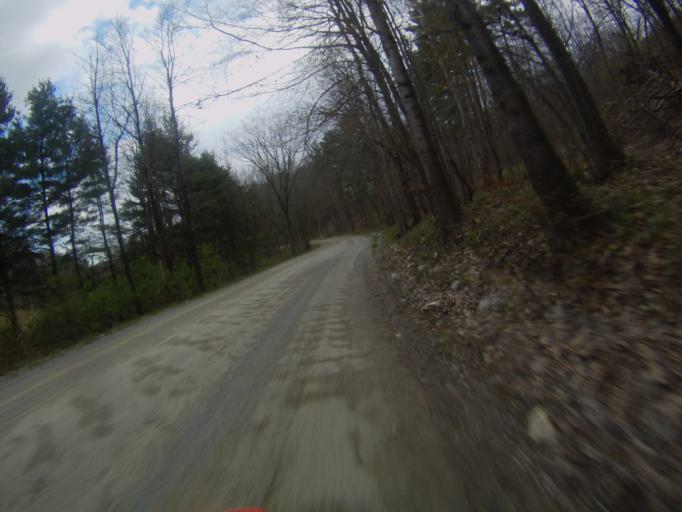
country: US
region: Vermont
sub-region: Addison County
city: Middlebury (village)
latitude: 43.9795
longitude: -73.0634
